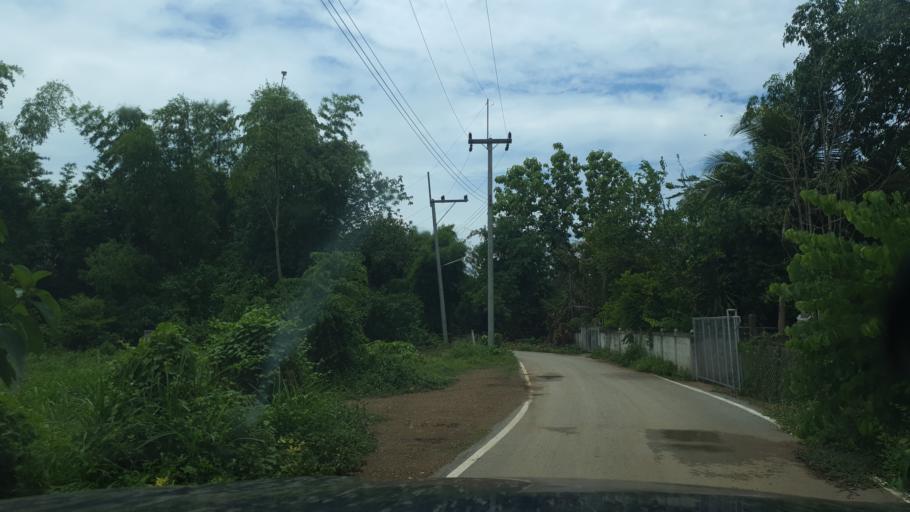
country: TH
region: Lampang
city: Ko Kha
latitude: 18.1264
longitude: 99.3486
